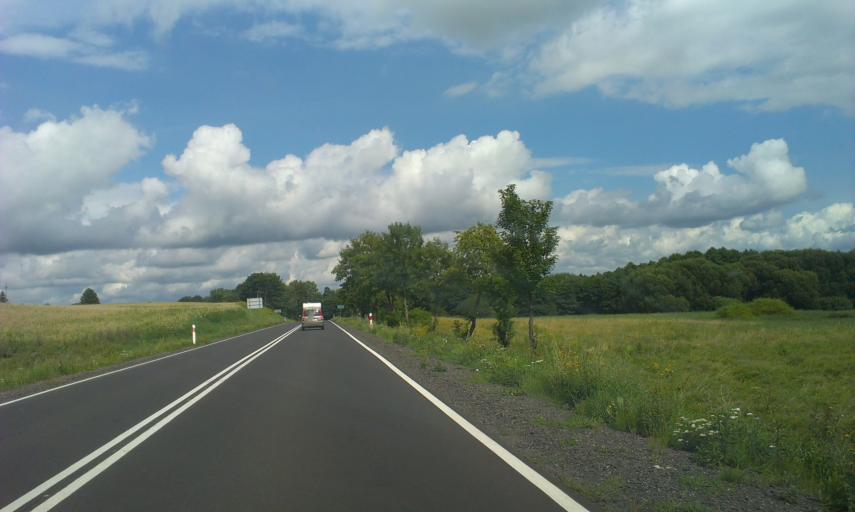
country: PL
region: West Pomeranian Voivodeship
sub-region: Powiat koszalinski
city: Bobolice
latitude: 53.9450
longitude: 16.5891
